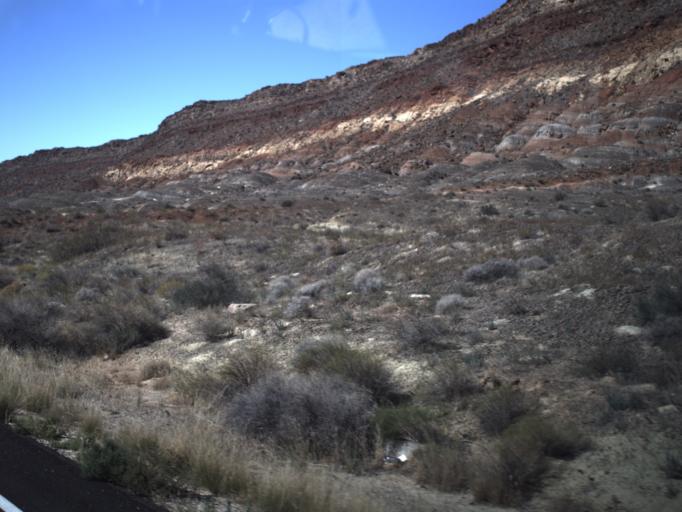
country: US
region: Utah
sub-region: Washington County
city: Washington
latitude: 37.1724
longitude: -113.4034
